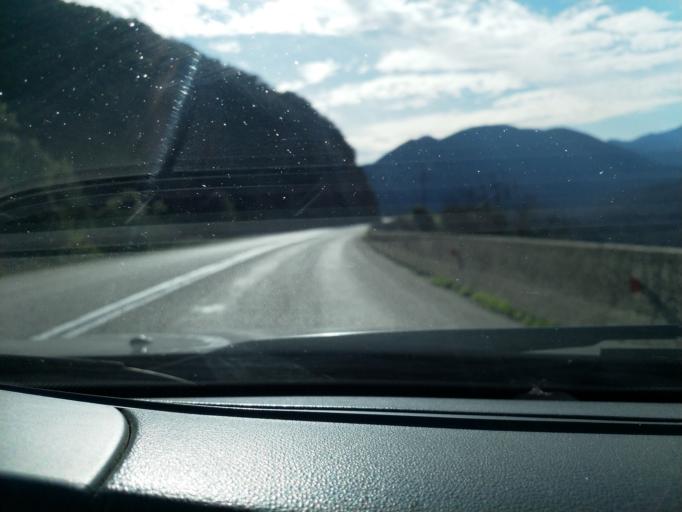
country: GR
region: Epirus
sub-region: Nomos Ioanninon
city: Agia Kyriaki
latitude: 39.4799
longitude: 20.8750
